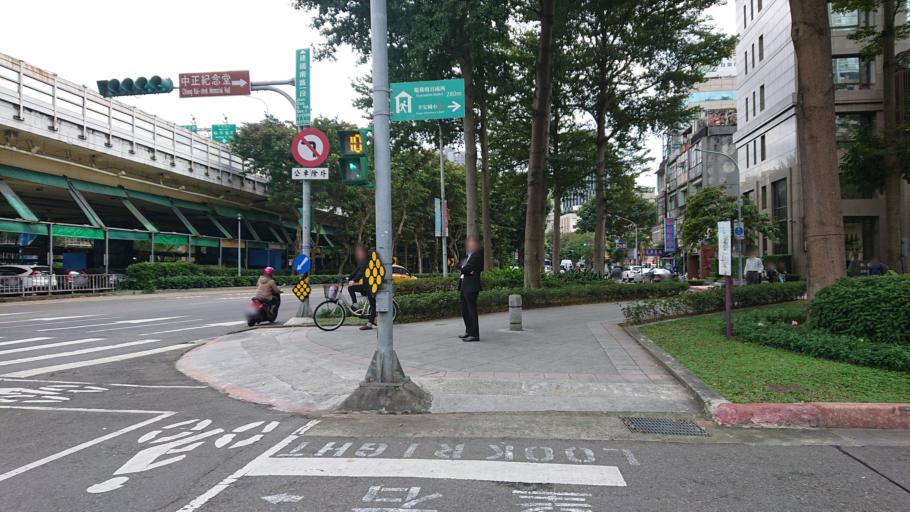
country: TW
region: Taipei
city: Taipei
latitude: 25.0380
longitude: 121.5375
